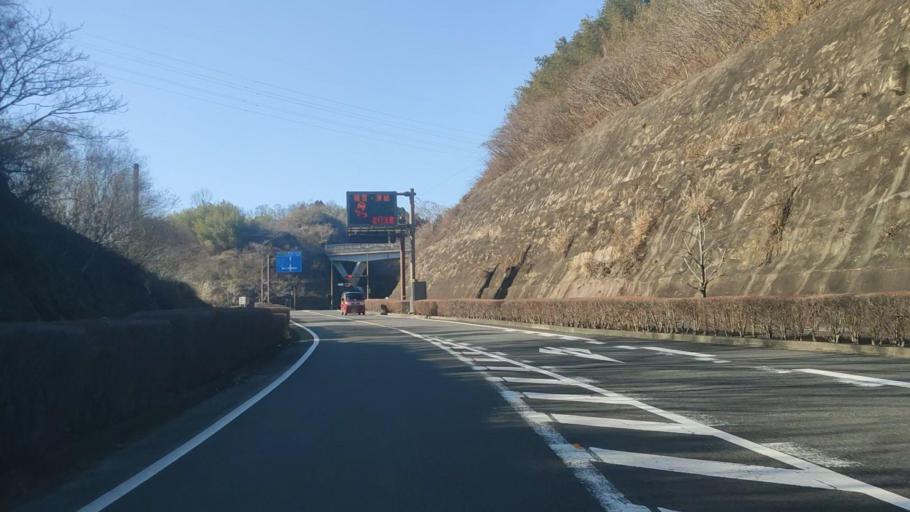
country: JP
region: Oita
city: Oita
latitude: 33.0706
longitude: 131.6330
